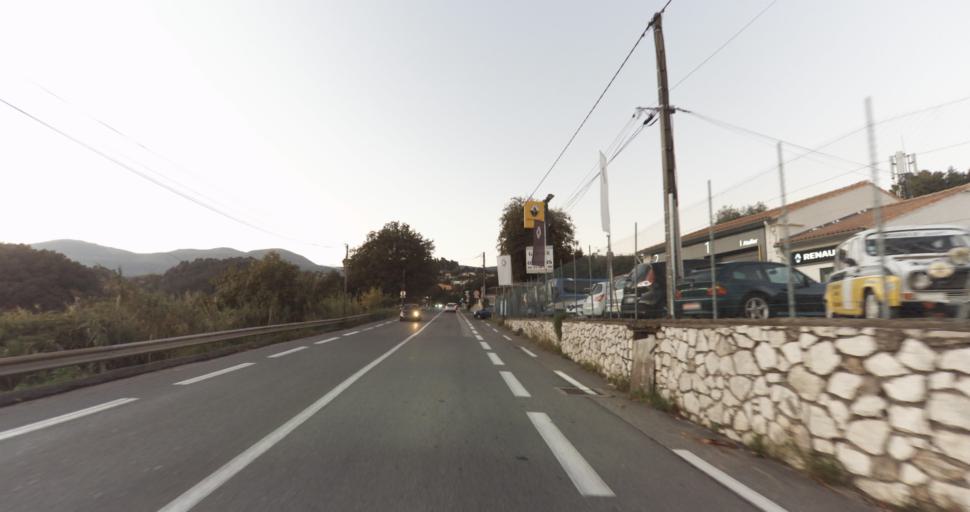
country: FR
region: Provence-Alpes-Cote d'Azur
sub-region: Departement des Alpes-Maritimes
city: Saint-Paul-de-Vence
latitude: 43.7095
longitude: 7.1272
